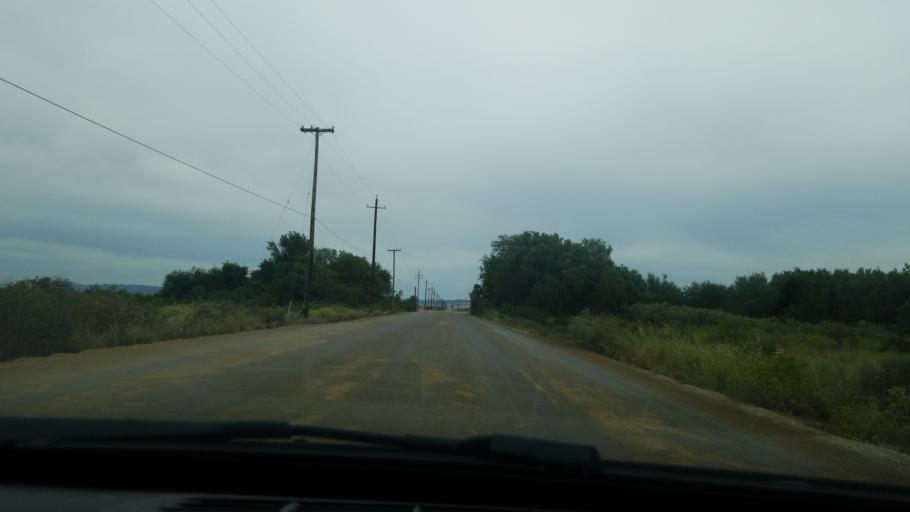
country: US
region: California
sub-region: Santa Barbara County
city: Guadalupe
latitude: 34.9821
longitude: -120.5129
